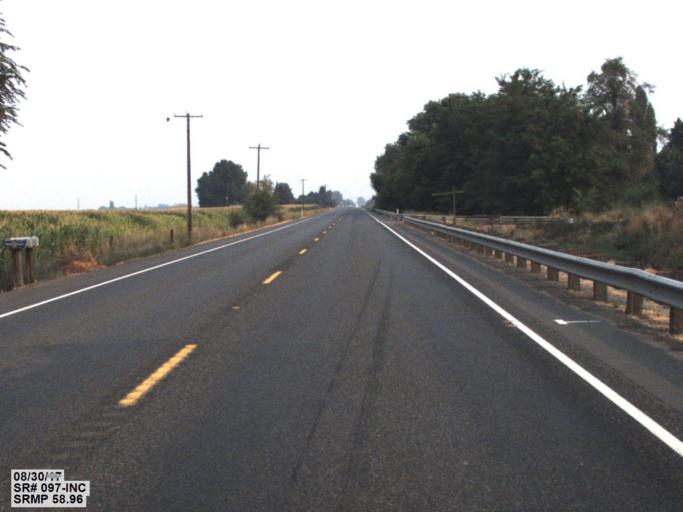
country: US
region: Washington
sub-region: Yakima County
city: Toppenish
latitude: 46.3342
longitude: -120.3205
